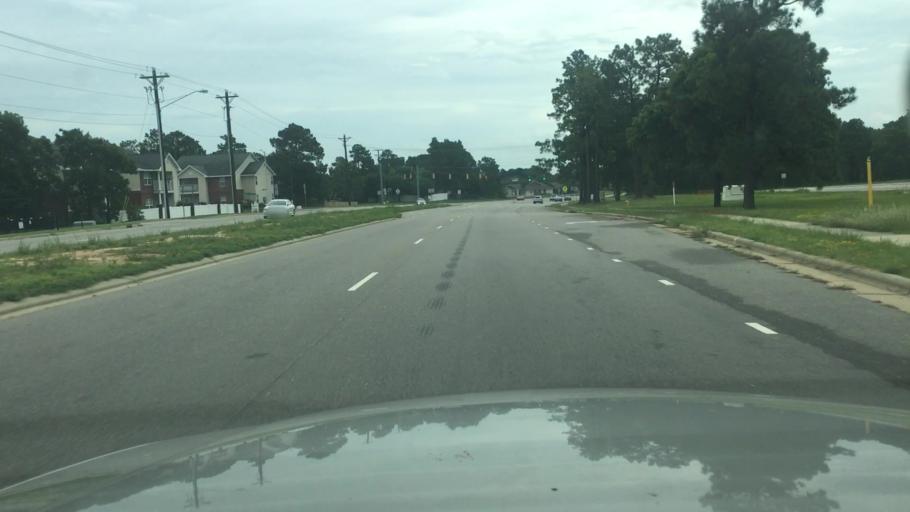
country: US
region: North Carolina
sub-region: Cumberland County
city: Hope Mills
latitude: 34.9794
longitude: -78.9256
